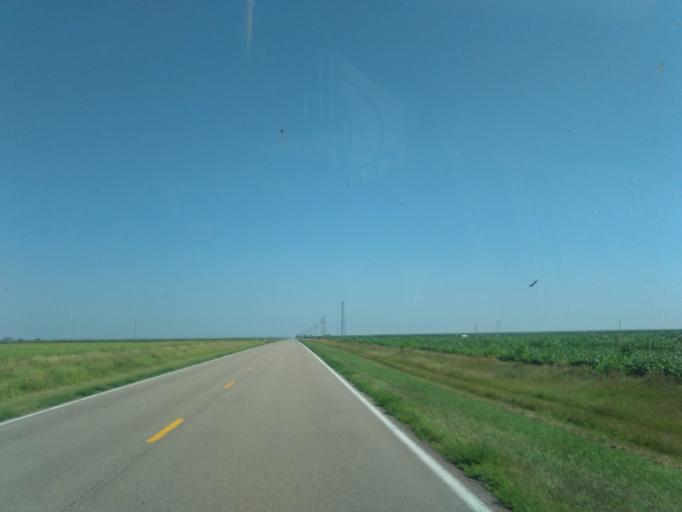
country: US
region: Kansas
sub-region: Cheyenne County
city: Saint Francis
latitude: 39.7687
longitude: -101.5421
